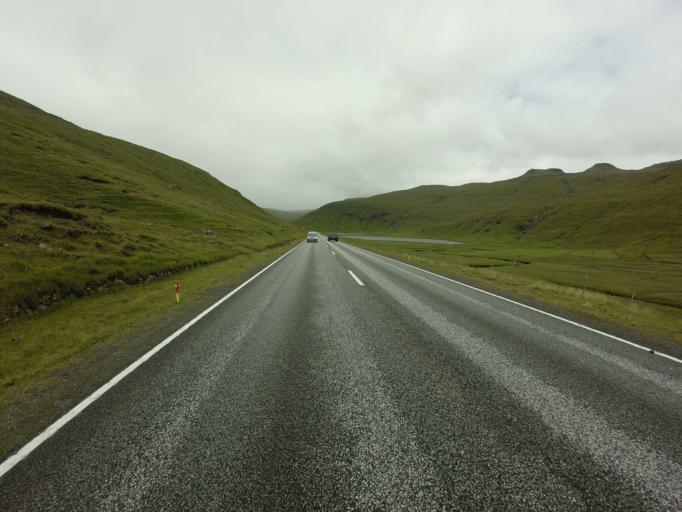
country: FO
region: Streymoy
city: Kollafjordhur
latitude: 62.1221
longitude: -6.9902
